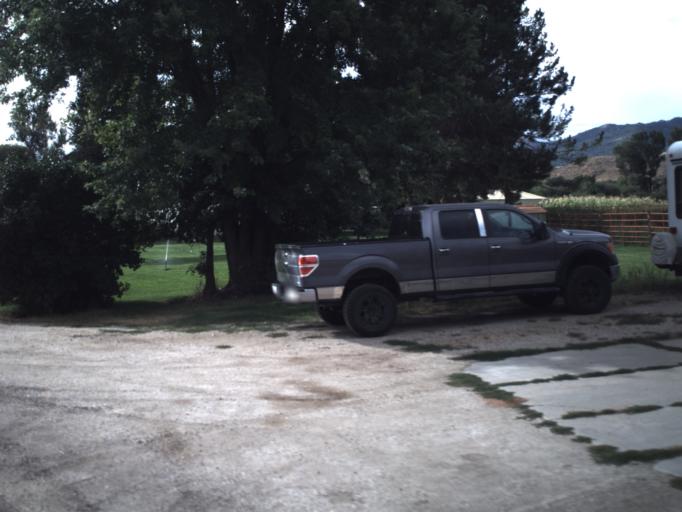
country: US
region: Utah
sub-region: Morgan County
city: Morgan
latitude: 40.9779
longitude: -111.6750
